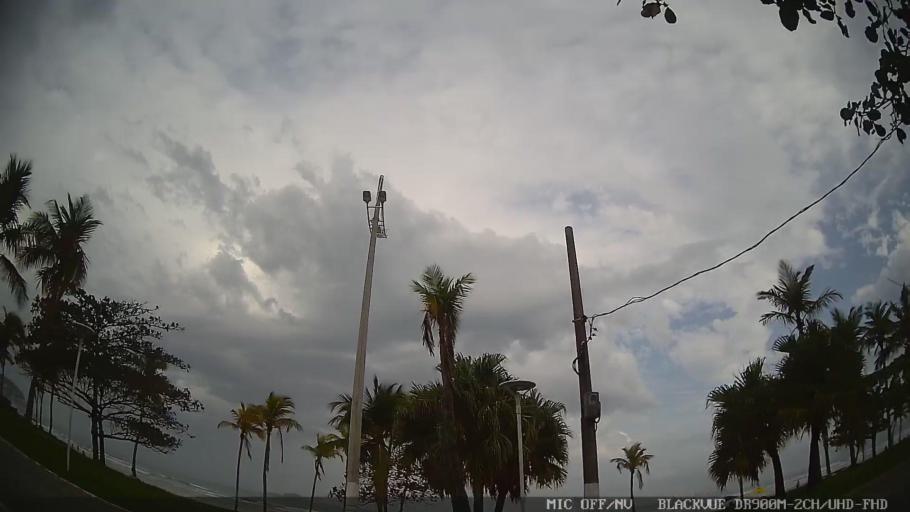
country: BR
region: Sao Paulo
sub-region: Guaruja
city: Guaruja
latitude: -23.9863
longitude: -46.2276
